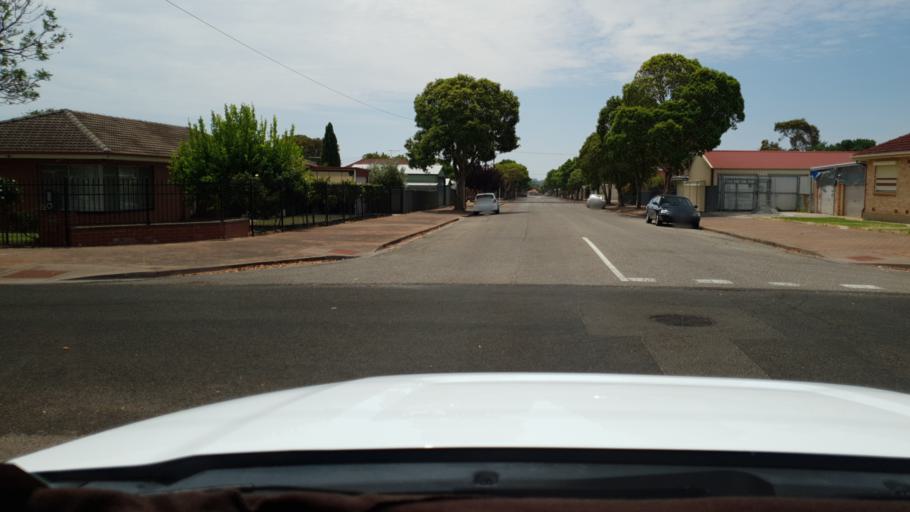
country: AU
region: South Australia
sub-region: Marion
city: Clovelly Park
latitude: -35.0048
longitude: 138.5794
